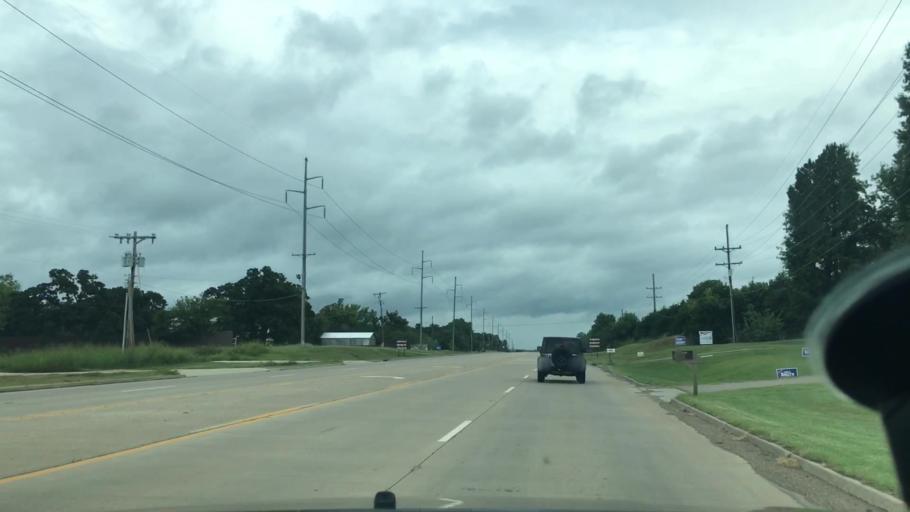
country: US
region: Oklahoma
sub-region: Seminole County
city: Seminole
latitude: 35.2576
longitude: -96.6712
